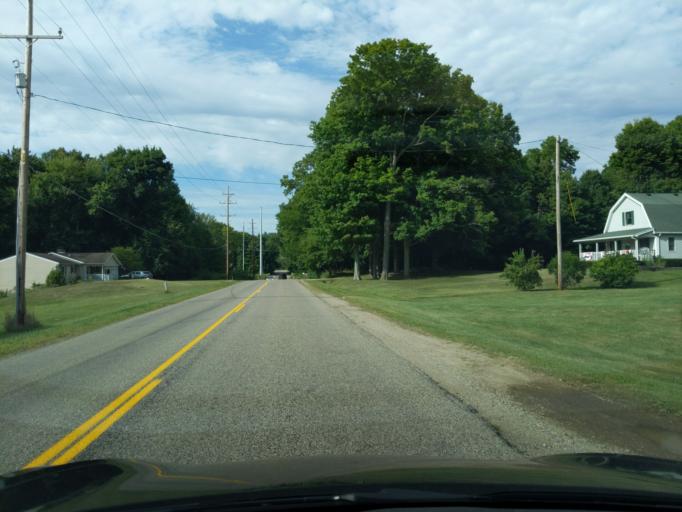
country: US
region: Michigan
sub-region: Eaton County
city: Dimondale
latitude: 42.6742
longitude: -84.6227
